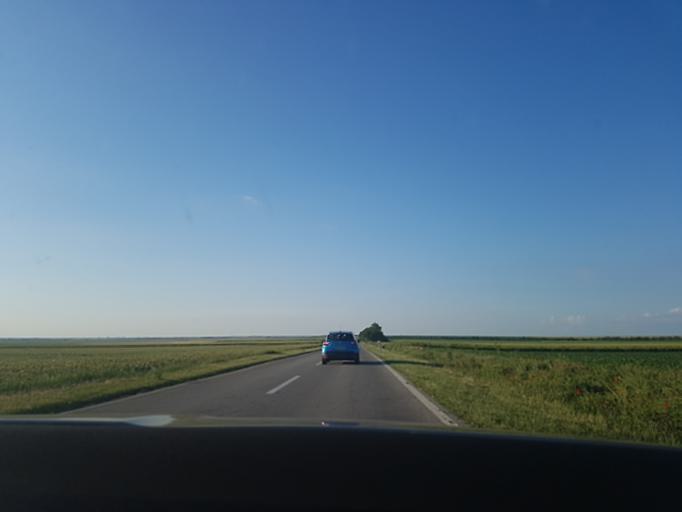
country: RS
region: Autonomna Pokrajina Vojvodina
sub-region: Juznobanatski Okrug
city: Vrsac
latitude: 45.1720
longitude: 21.2936
